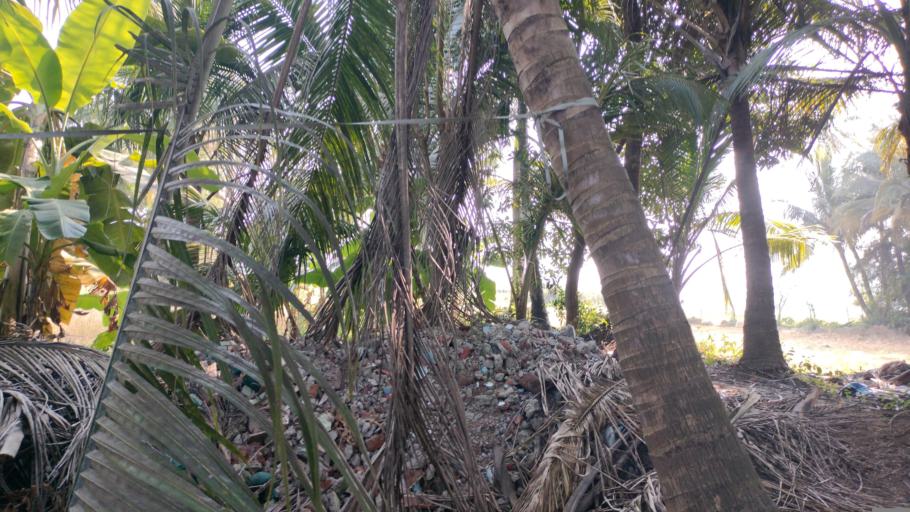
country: IN
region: Maharashtra
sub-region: Thane
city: Virar
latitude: 19.4014
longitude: 72.7967
